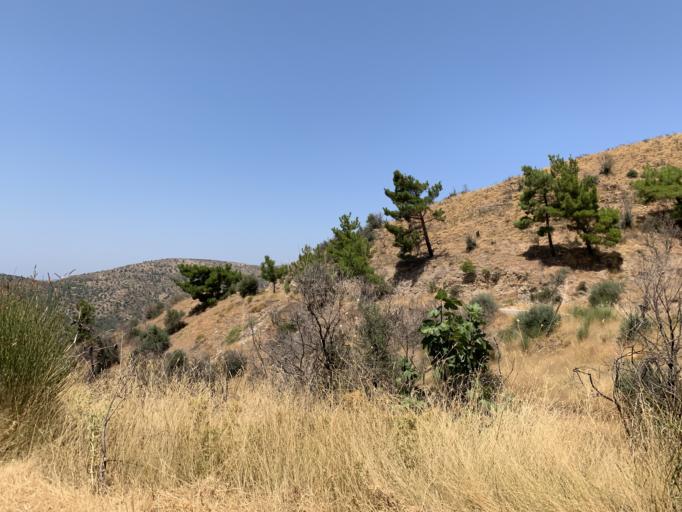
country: GR
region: North Aegean
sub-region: Chios
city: Vrontados
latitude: 38.4426
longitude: 25.9776
